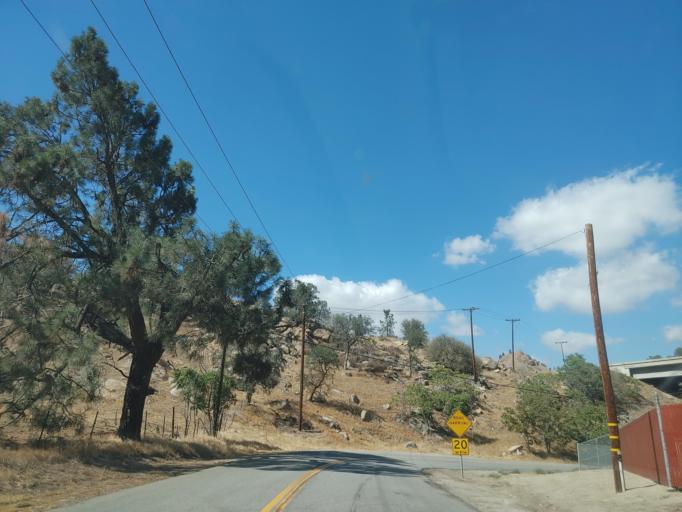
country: US
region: California
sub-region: Kern County
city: Bear Valley Springs
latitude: 35.2198
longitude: -118.5580
